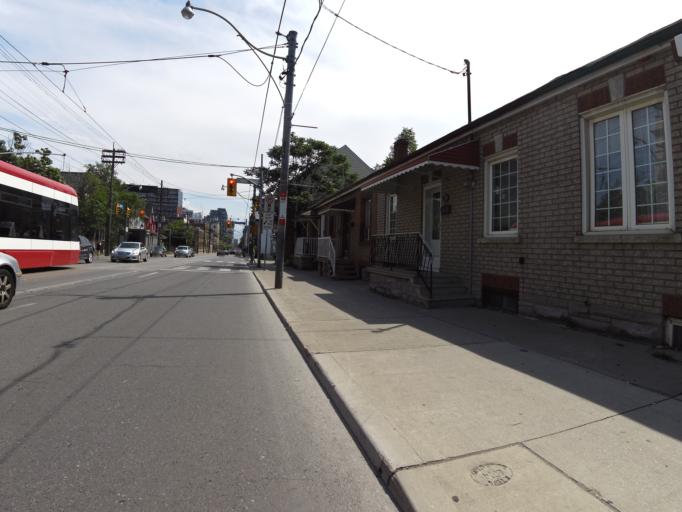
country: CA
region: Ontario
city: Toronto
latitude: 43.6491
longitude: -79.4049
